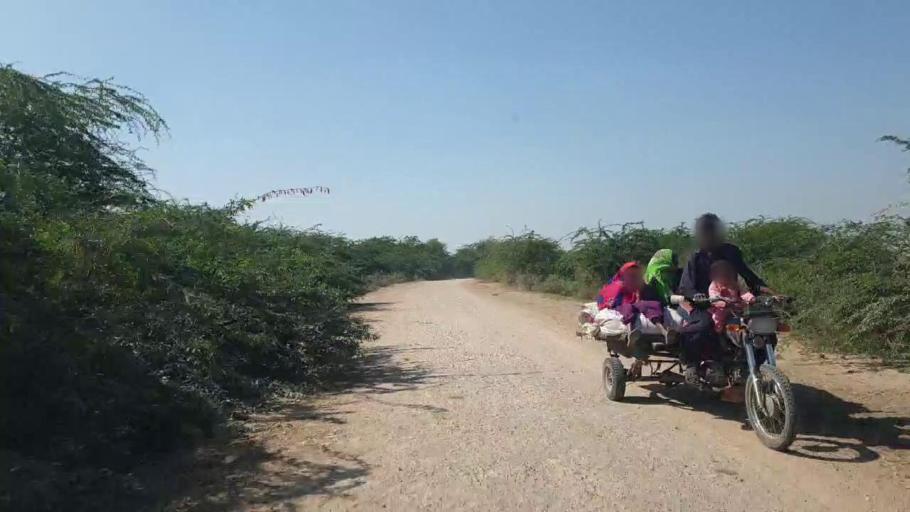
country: PK
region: Sindh
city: Talhar
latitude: 24.8293
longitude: 68.7853
